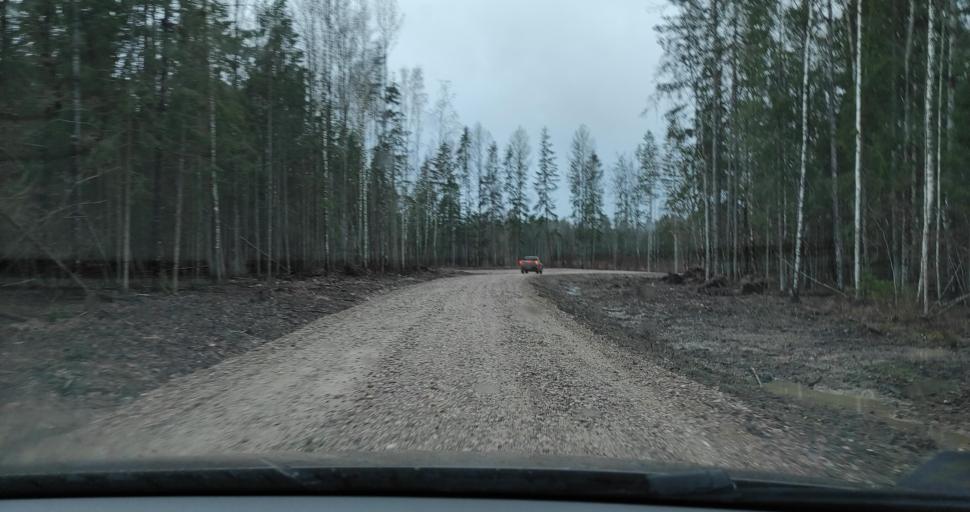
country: LV
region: Skrunda
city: Skrunda
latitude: 56.5573
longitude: 22.0485
